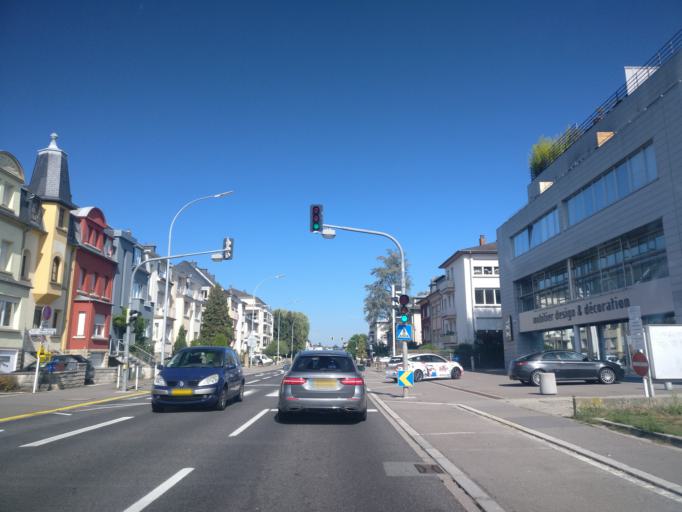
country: LU
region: Luxembourg
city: Bereldange
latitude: 49.6534
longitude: 6.1275
